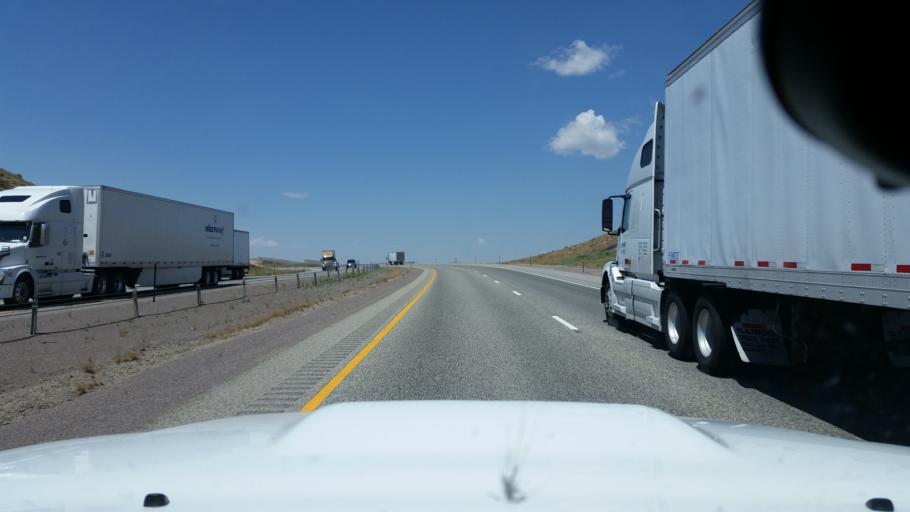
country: US
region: Wyoming
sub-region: Carbon County
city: Saratoga
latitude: 41.7528
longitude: -106.5101
